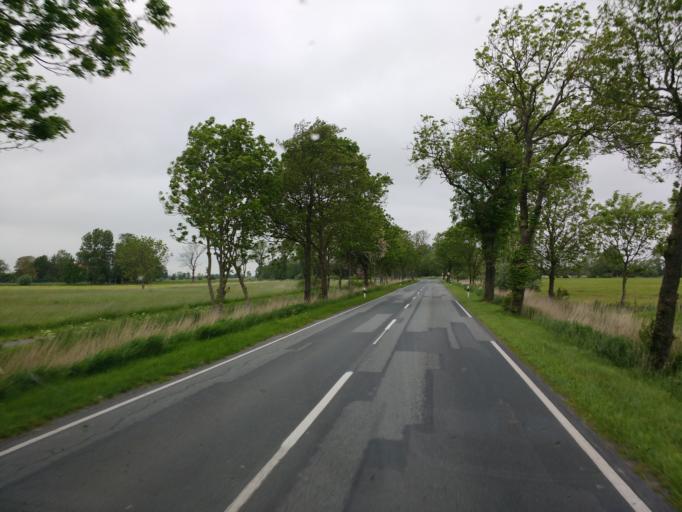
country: DE
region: Lower Saxony
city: Jever
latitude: 53.6244
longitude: 7.9287
